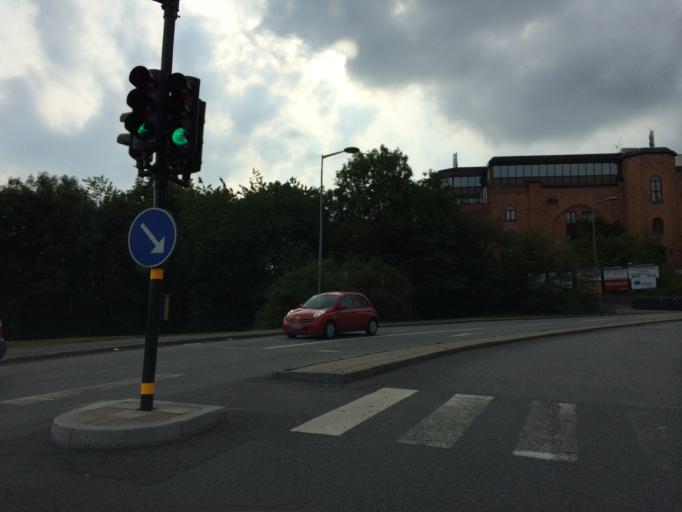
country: SE
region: Stockholm
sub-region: Stockholms Kommun
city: Arsta
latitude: 59.3093
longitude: 18.0244
